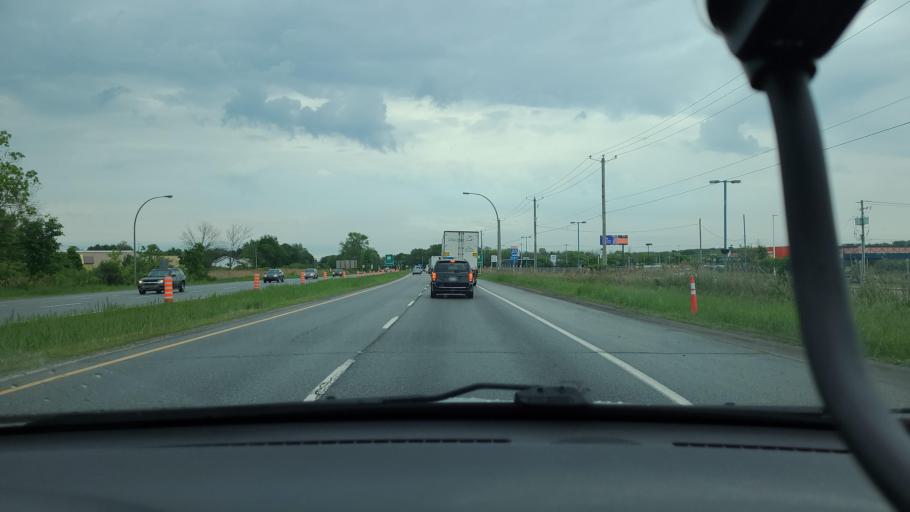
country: CA
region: Quebec
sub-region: Monteregie
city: Pincourt
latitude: 45.3868
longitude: -73.9888
